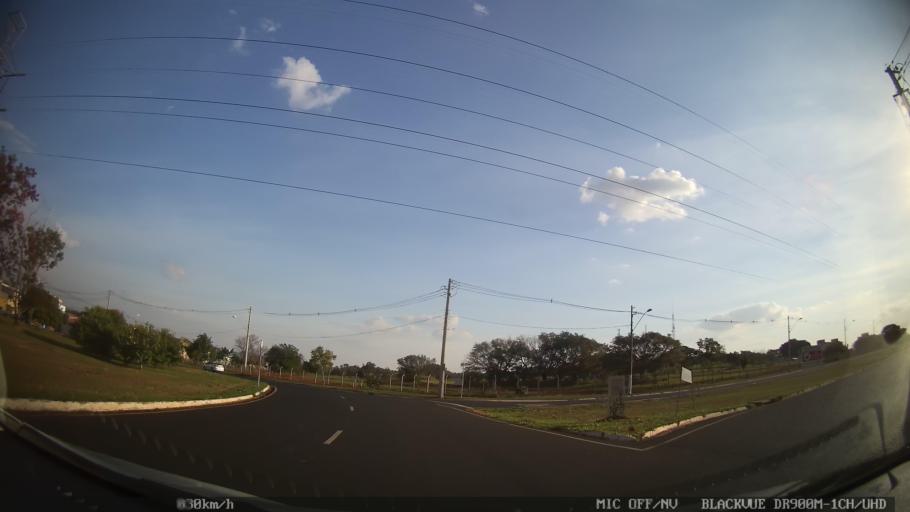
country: BR
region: Sao Paulo
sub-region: Ribeirao Preto
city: Ribeirao Preto
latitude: -21.1602
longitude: -47.8420
